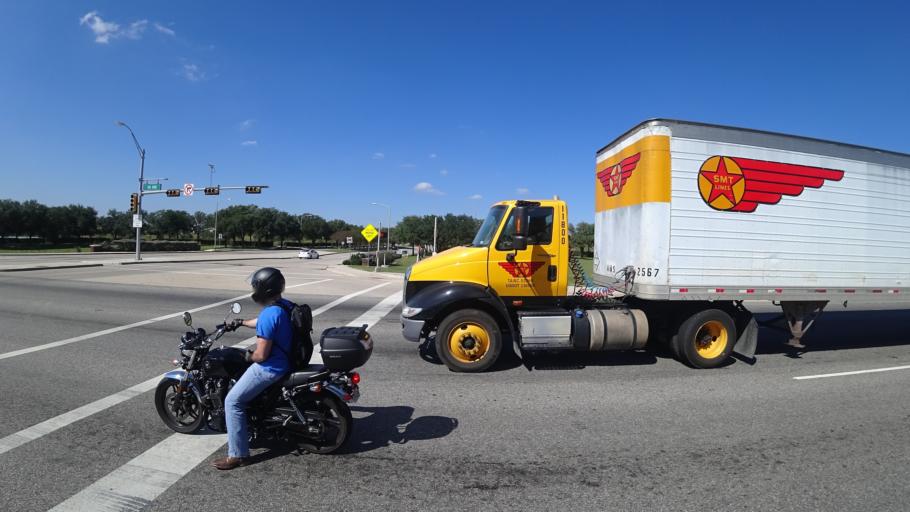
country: US
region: Texas
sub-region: Travis County
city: Manor
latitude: 30.3351
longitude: -97.6073
